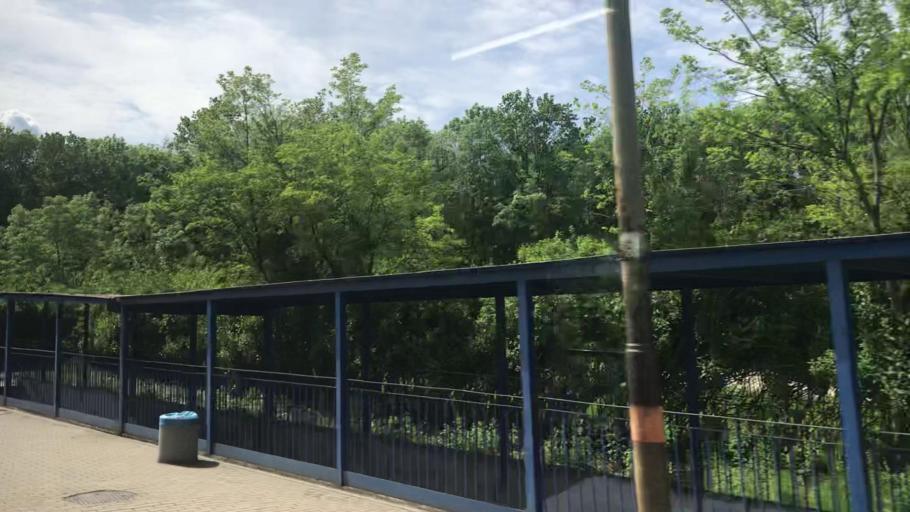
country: PL
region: Lower Silesian Voivodeship
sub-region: Powiat wroclawski
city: Katy Wroclawskie
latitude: 50.9869
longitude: 16.6603
